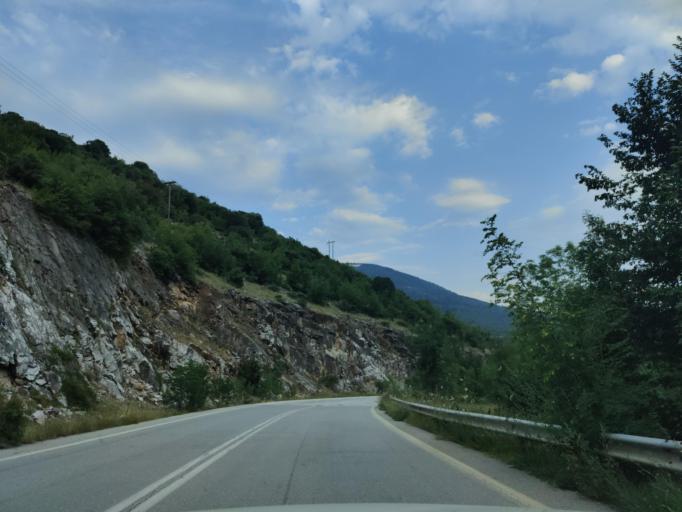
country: GR
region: East Macedonia and Thrace
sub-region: Nomos Dramas
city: Volakas
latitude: 41.2831
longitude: 23.9735
